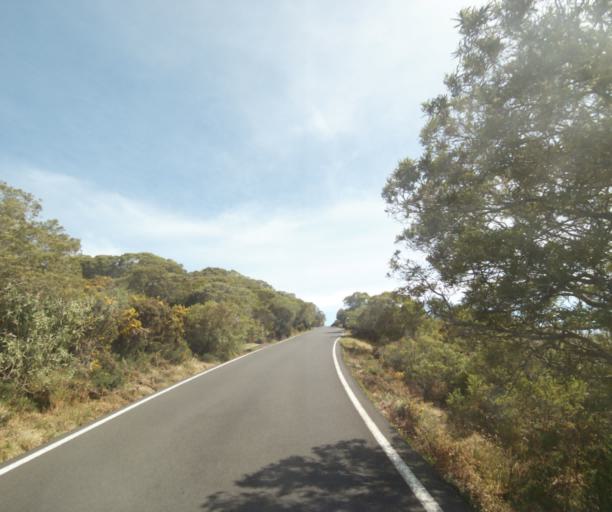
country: RE
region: Reunion
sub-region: Reunion
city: Trois-Bassins
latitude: -21.0707
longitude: 55.3791
